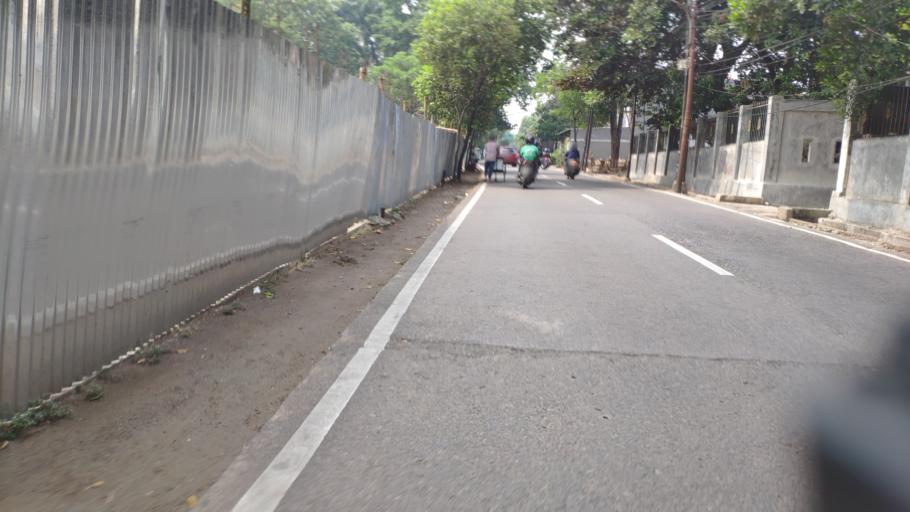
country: ID
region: West Java
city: Pamulang
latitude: -6.3142
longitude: 106.8163
